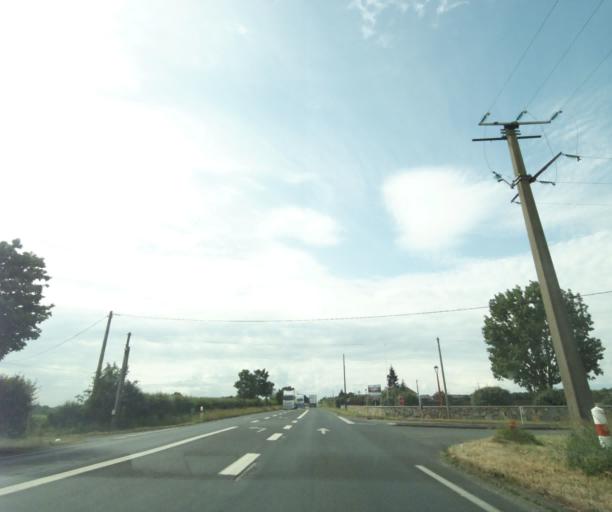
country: FR
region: Pays de la Loire
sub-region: Departement de la Sarthe
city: Solesmes
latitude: 47.8158
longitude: -0.2896
